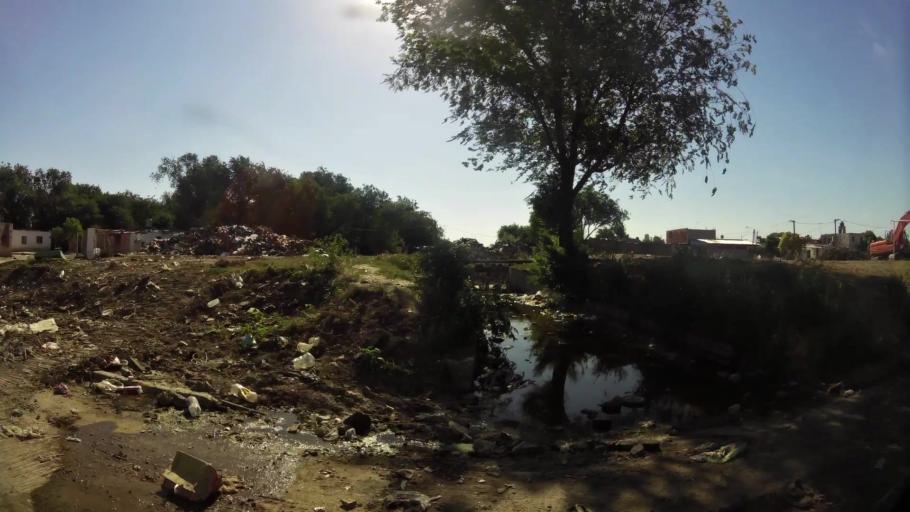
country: AR
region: Cordoba
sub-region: Departamento de Capital
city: Cordoba
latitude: -31.3744
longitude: -64.1892
